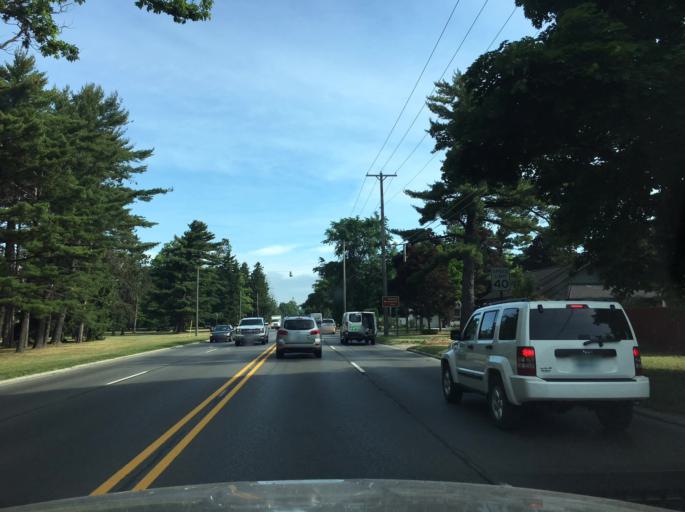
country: US
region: Michigan
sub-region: Grand Traverse County
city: Traverse City
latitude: 44.7540
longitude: -85.6349
